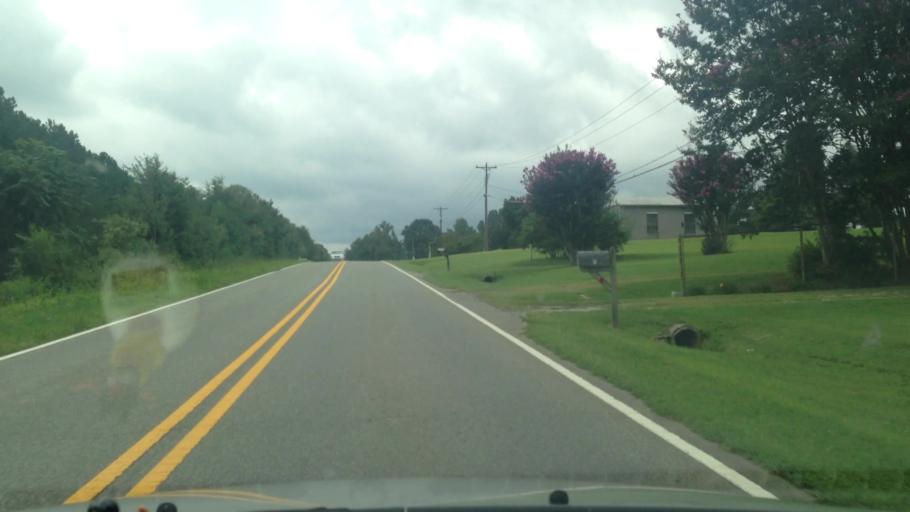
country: US
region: North Carolina
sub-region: Stokes County
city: Walnut Cove
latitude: 36.2656
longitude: -80.1461
